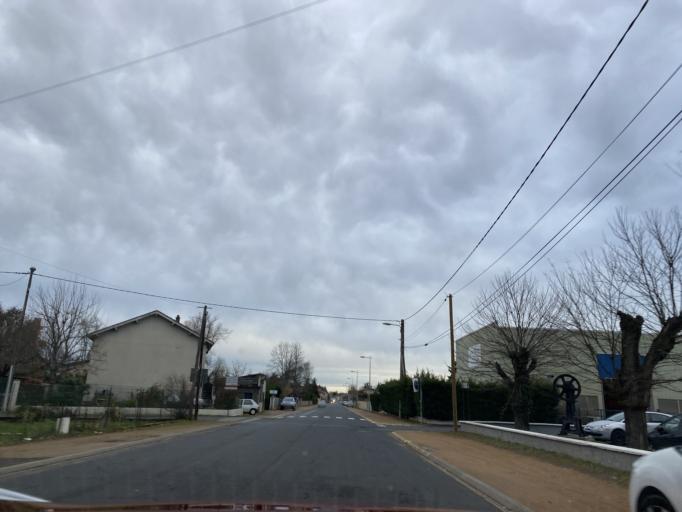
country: FR
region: Auvergne
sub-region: Departement du Puy-de-Dome
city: Peschadoires
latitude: 45.8315
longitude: 3.5007
